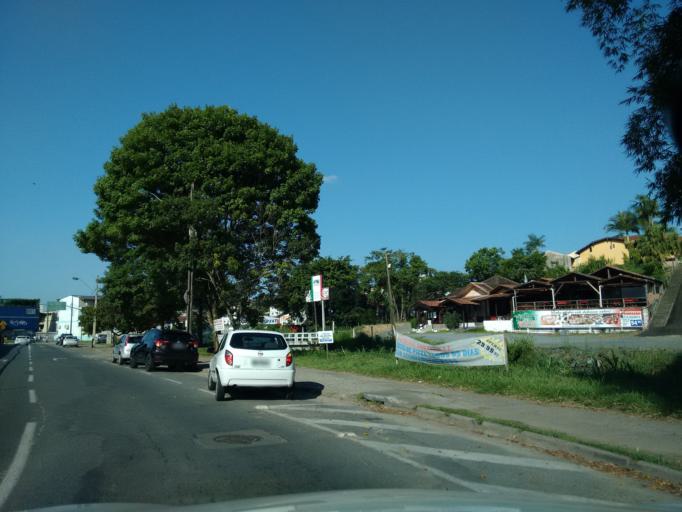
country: BR
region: Santa Catarina
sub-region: Blumenau
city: Blumenau
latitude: -26.8807
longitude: -49.0678
